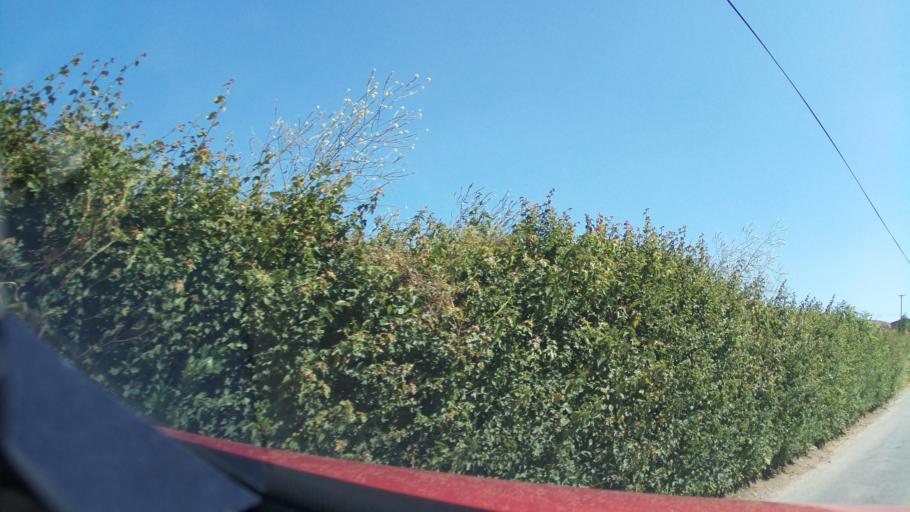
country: GB
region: England
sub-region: Devon
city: Ipplepen
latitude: 50.4883
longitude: -3.6249
